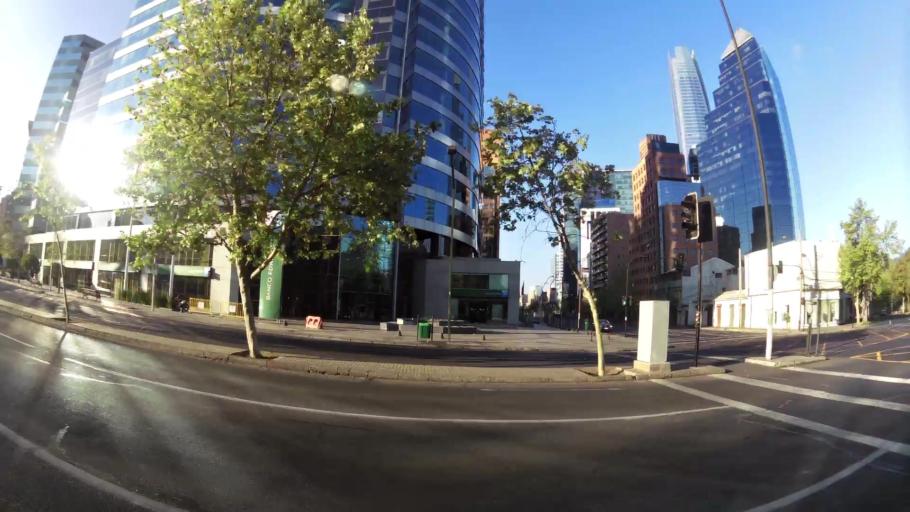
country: CL
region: Santiago Metropolitan
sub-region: Provincia de Santiago
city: Villa Presidente Frei, Nunoa, Santiago, Chile
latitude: -33.4137
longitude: -70.6034
